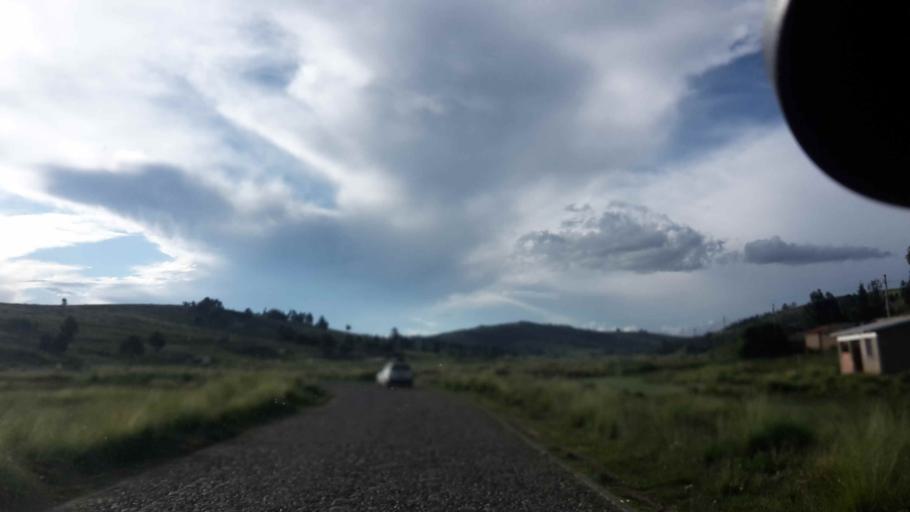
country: BO
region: Cochabamba
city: Arani
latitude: -17.5311
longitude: -65.6581
